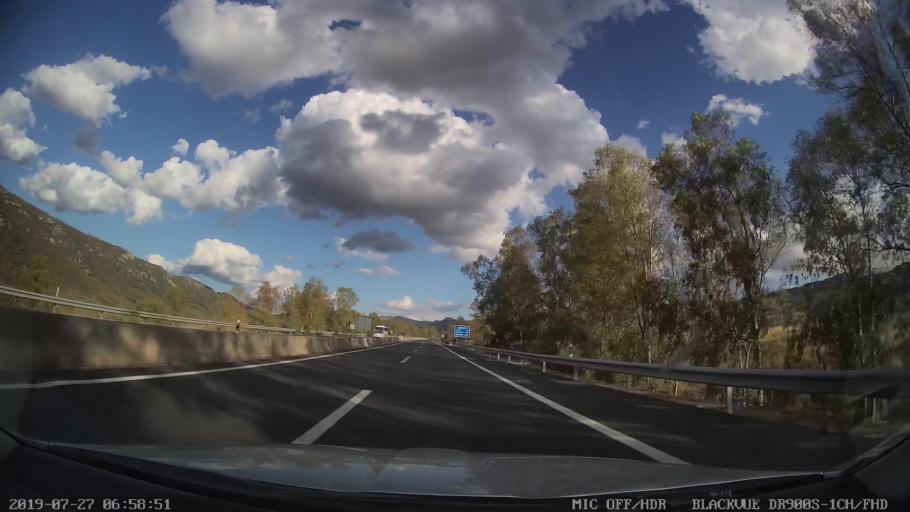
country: ES
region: Extremadura
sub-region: Provincia de Caceres
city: Romangordo
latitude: 39.7252
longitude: -5.7147
